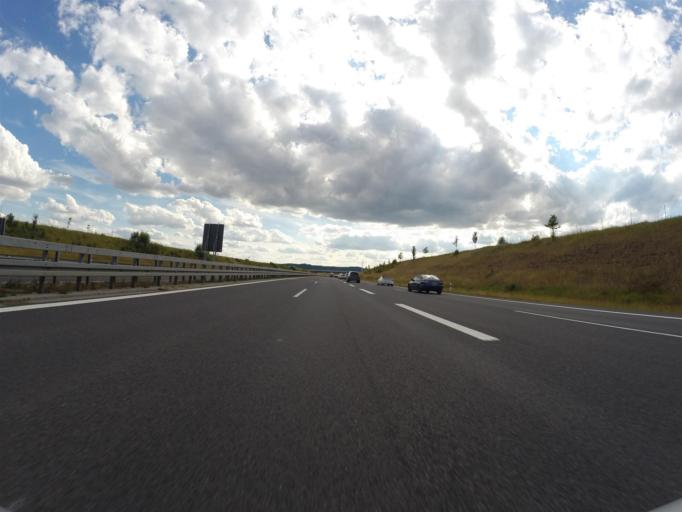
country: DE
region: Bavaria
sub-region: Upper Franconia
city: Coburg
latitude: 50.2941
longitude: 10.9892
